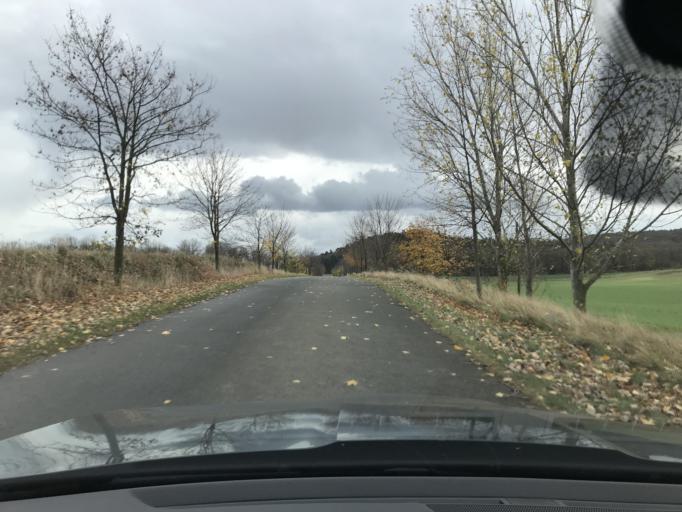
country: DE
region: Saxony-Anhalt
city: Langenstein
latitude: 51.8481
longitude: 11.0116
